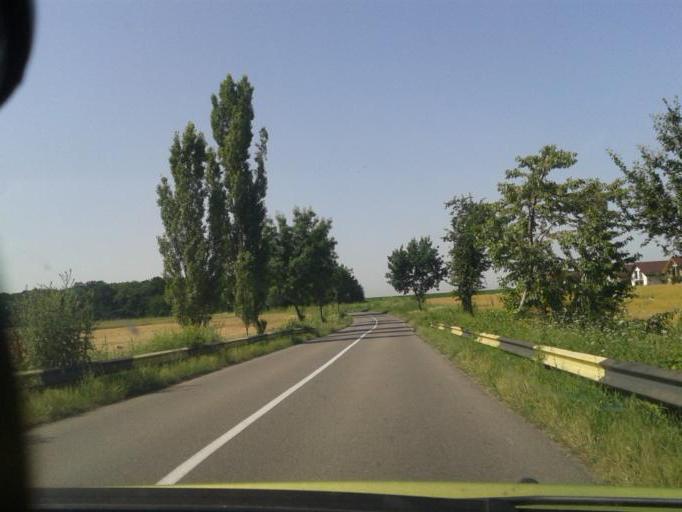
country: RO
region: Prahova
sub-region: Comuna Paulesti
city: Gageni
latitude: 44.9985
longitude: 25.9436
